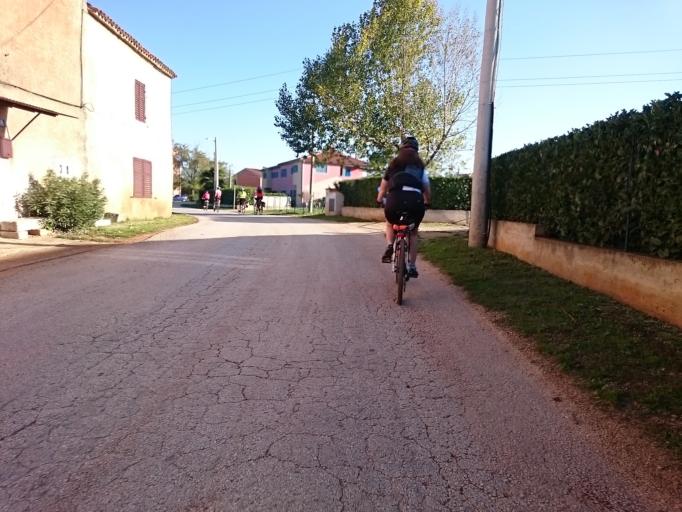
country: HR
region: Istarska
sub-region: Grad Porec
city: Porec
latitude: 45.2655
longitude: 13.6570
